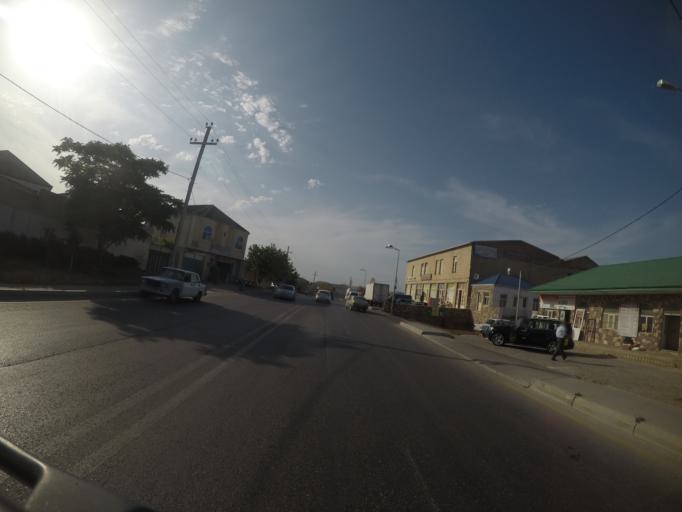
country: AZ
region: Baki
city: Binagadi
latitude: 40.4746
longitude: 49.8338
